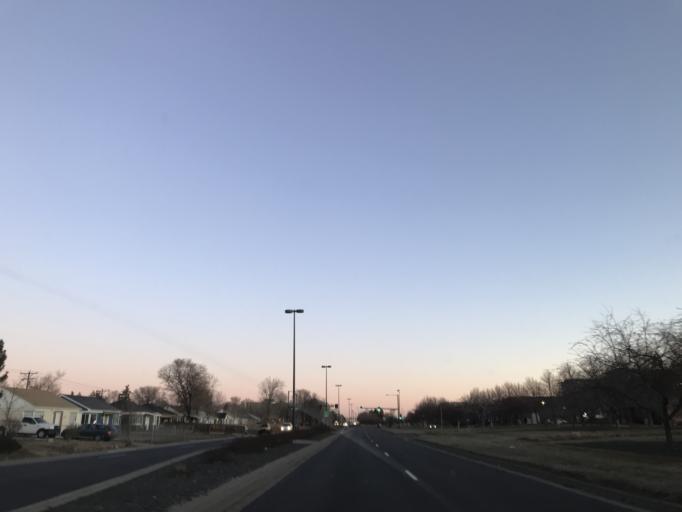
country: US
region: Colorado
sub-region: Arapahoe County
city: Glendale
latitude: 39.7564
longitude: -104.9033
